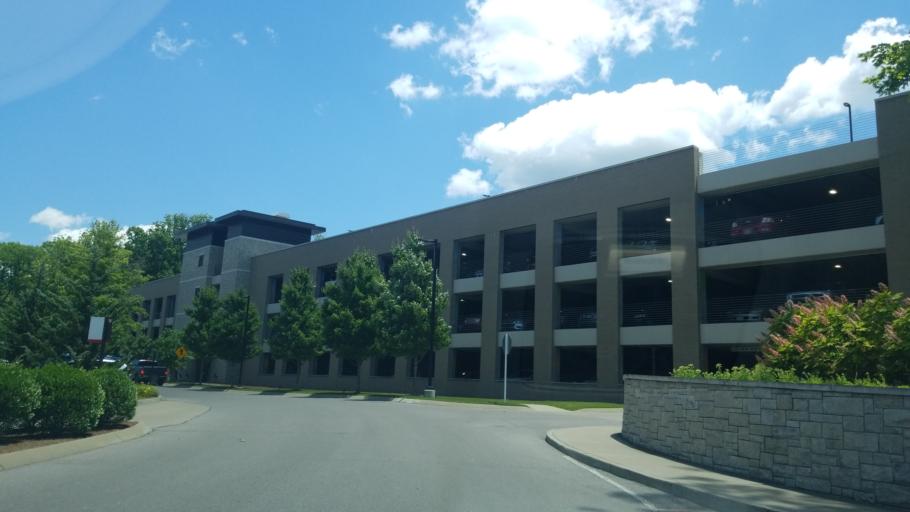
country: US
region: Tennessee
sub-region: Williamson County
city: Brentwood
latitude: 36.0315
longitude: -86.8133
